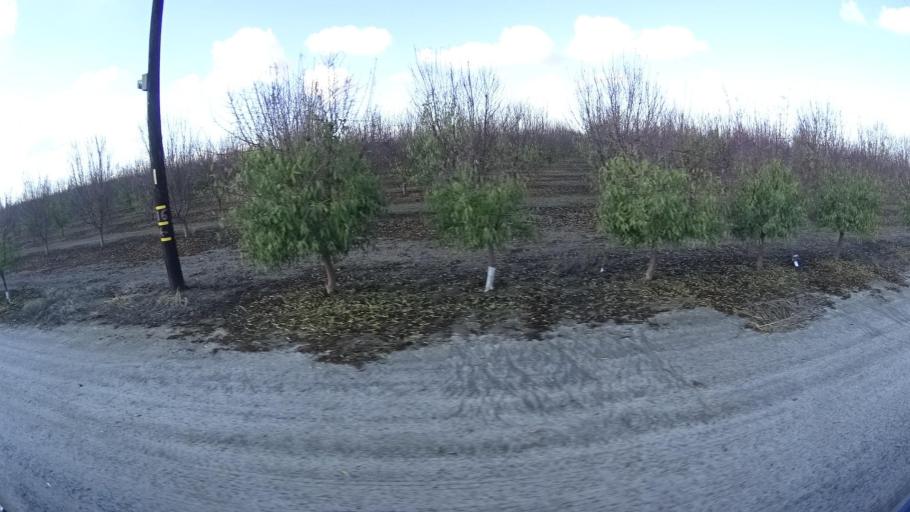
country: US
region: California
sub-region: Kern County
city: McFarland
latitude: 35.6610
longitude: -119.2588
